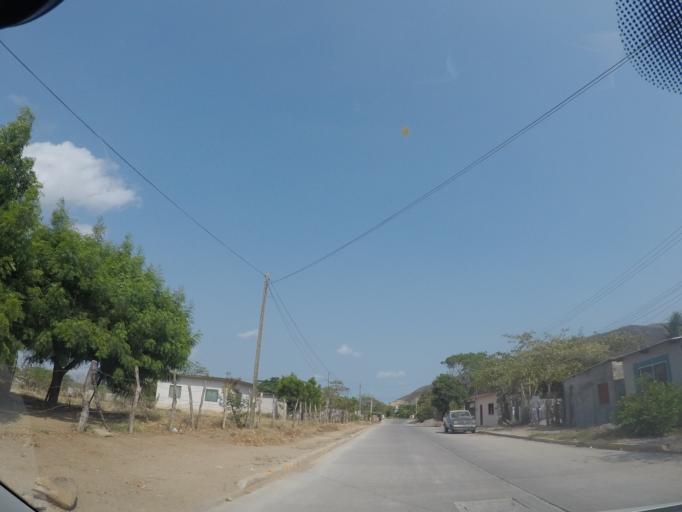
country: MX
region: Oaxaca
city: San Jeronimo Ixtepec
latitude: 16.5421
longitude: -95.0876
